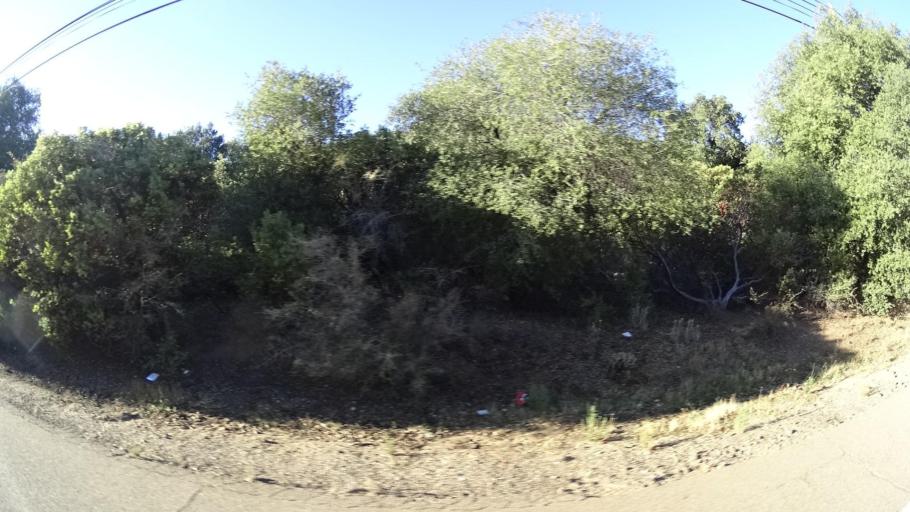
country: US
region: California
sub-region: San Diego County
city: Pine Valley
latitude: 32.8522
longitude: -116.5653
